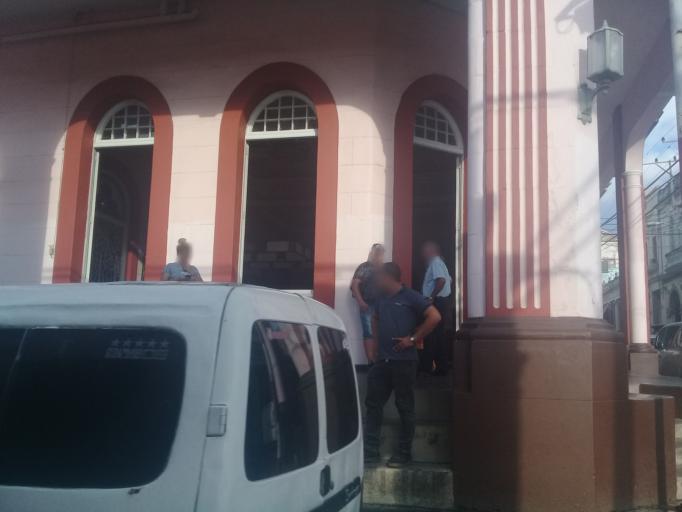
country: CU
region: Pinar del Rio
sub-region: Municipio de Pinar del Rio
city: Pinar del Rio
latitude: 22.4164
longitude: -83.6985
